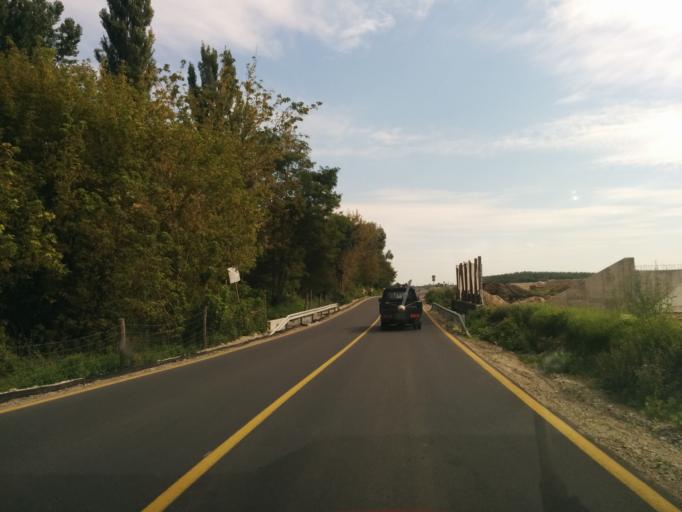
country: HU
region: Gyor-Moson-Sopron
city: Kony
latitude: 47.6299
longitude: 17.3270
